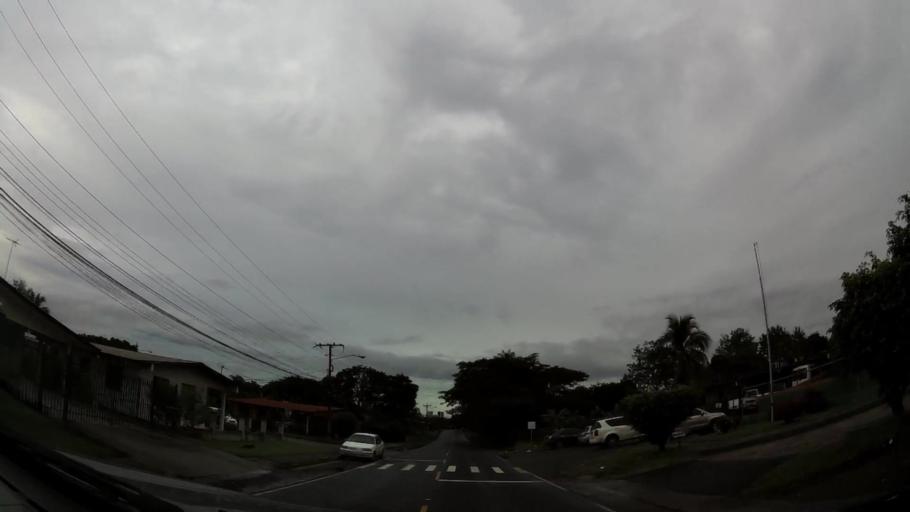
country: PA
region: Veraguas
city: Santiago de Veraguas
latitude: 8.1090
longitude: -80.9770
